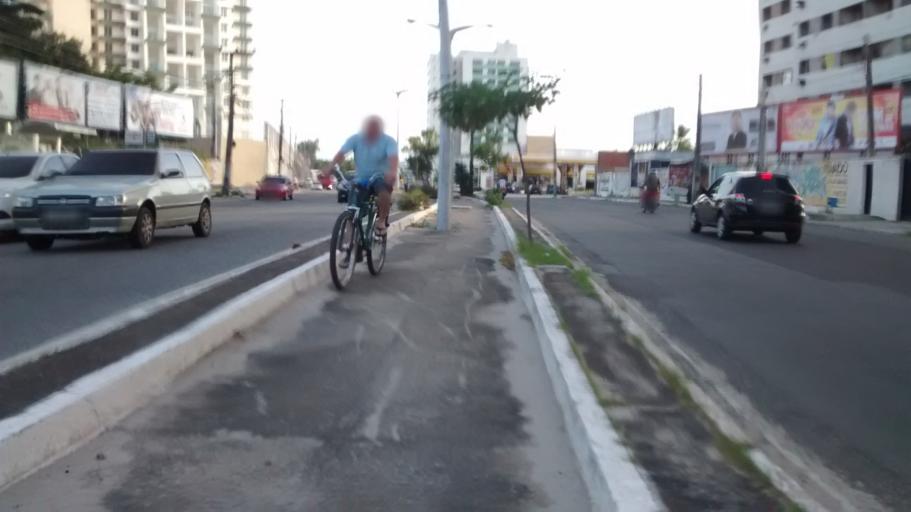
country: BR
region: Ceara
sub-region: Fortaleza
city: Fortaleza
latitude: -3.7652
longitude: -38.4957
